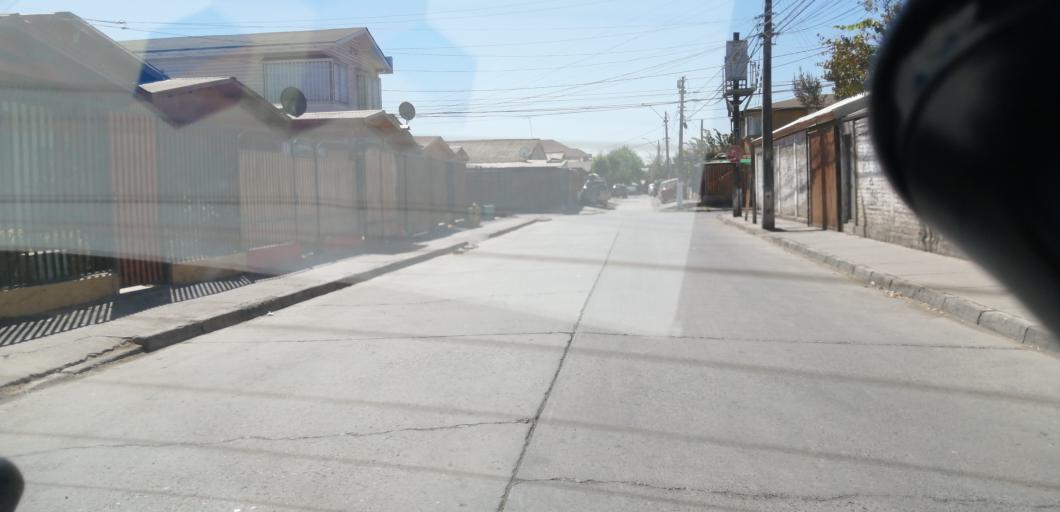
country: CL
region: Santiago Metropolitan
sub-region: Provincia de Santiago
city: Lo Prado
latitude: -33.4346
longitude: -70.7565
